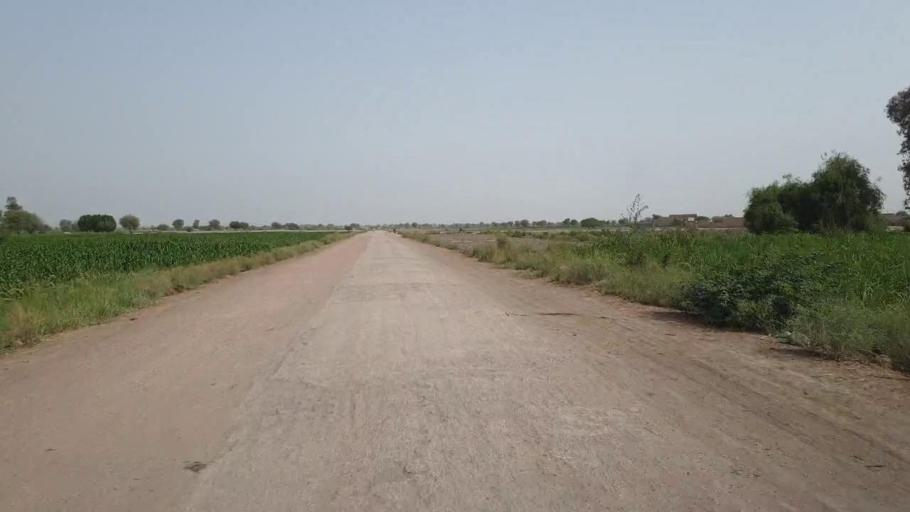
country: PK
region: Sindh
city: Daulatpur
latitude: 26.5536
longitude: 67.9908
